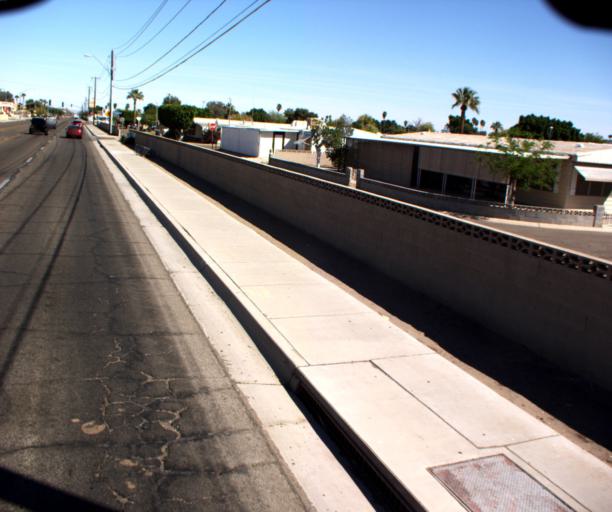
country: US
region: Arizona
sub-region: Yuma County
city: Yuma
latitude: 32.6890
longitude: -114.6503
